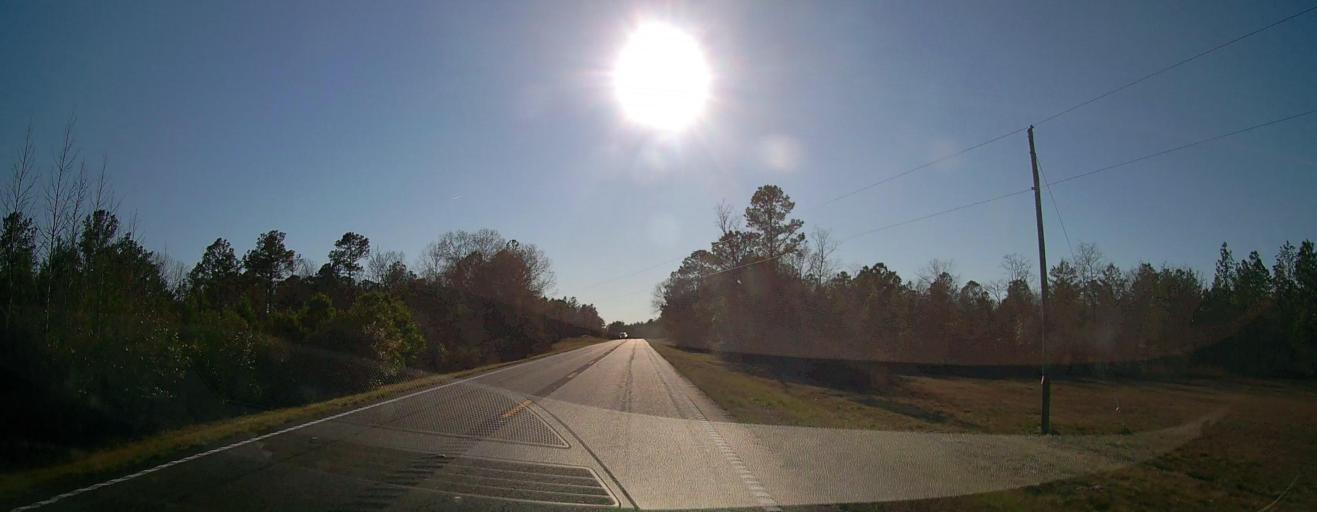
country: US
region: Georgia
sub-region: Taylor County
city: Butler
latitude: 32.5511
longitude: -84.2730
